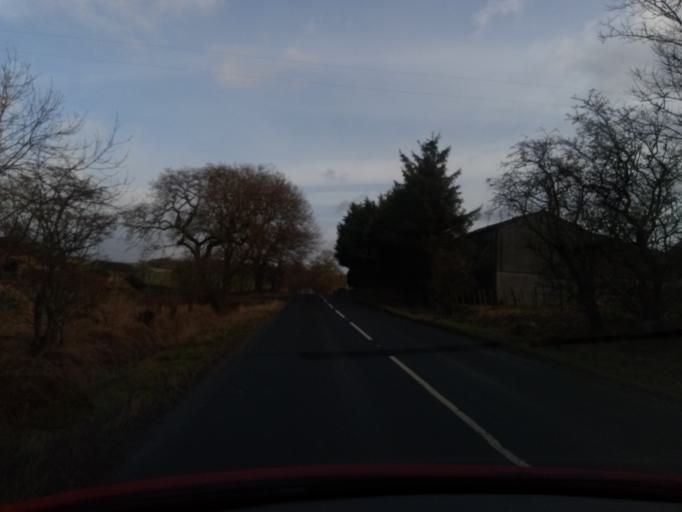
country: GB
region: England
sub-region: Northumberland
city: Corbridge
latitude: 55.1002
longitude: -2.0370
